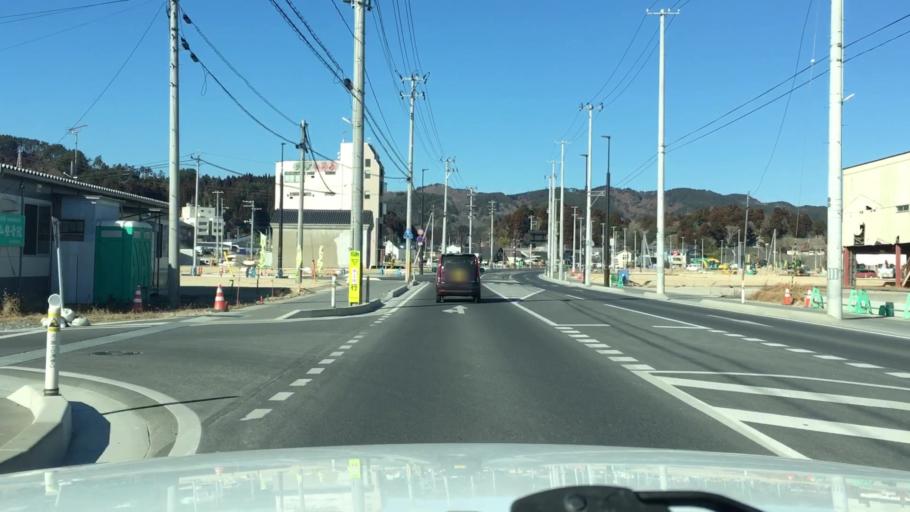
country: JP
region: Iwate
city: Yamada
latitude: 39.4641
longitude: 141.9533
